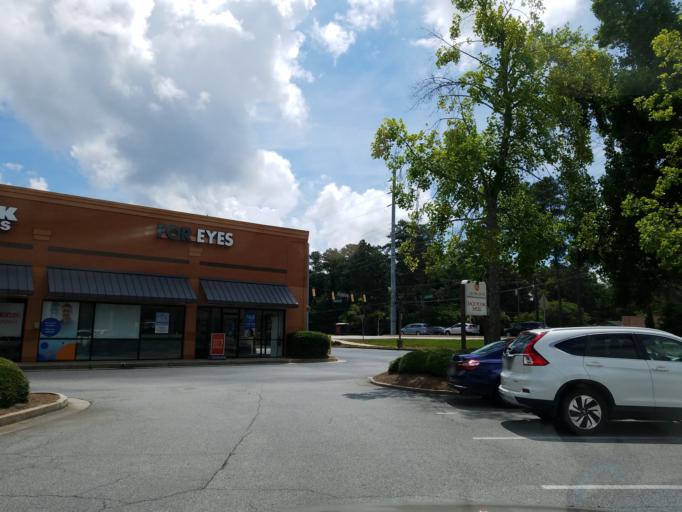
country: US
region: Georgia
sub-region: Fulton County
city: Sandy Springs
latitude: 33.9803
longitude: -84.4337
